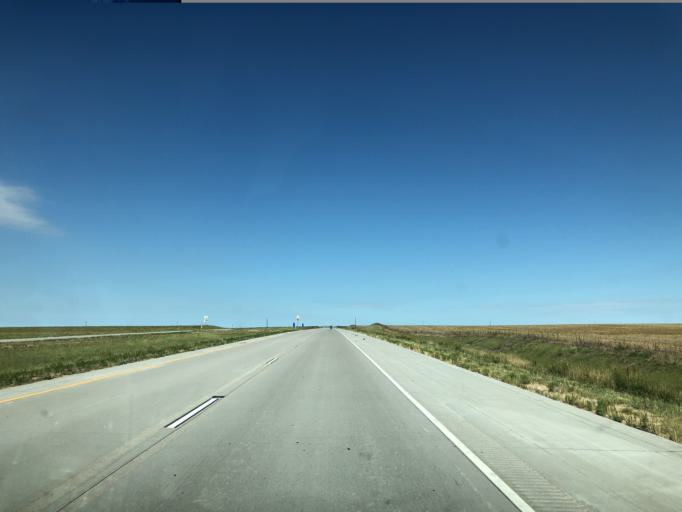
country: US
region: Colorado
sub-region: Kit Carson County
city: Burlington
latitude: 39.2941
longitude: -102.7546
